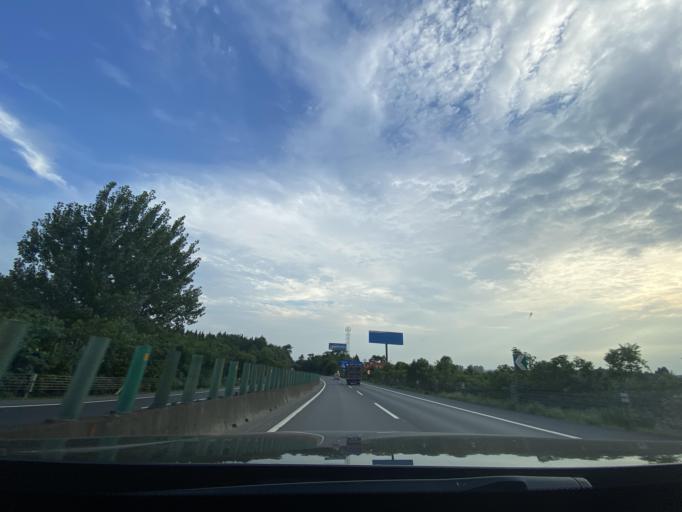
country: CN
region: Sichuan
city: Luojiang
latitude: 31.3905
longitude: 104.5566
